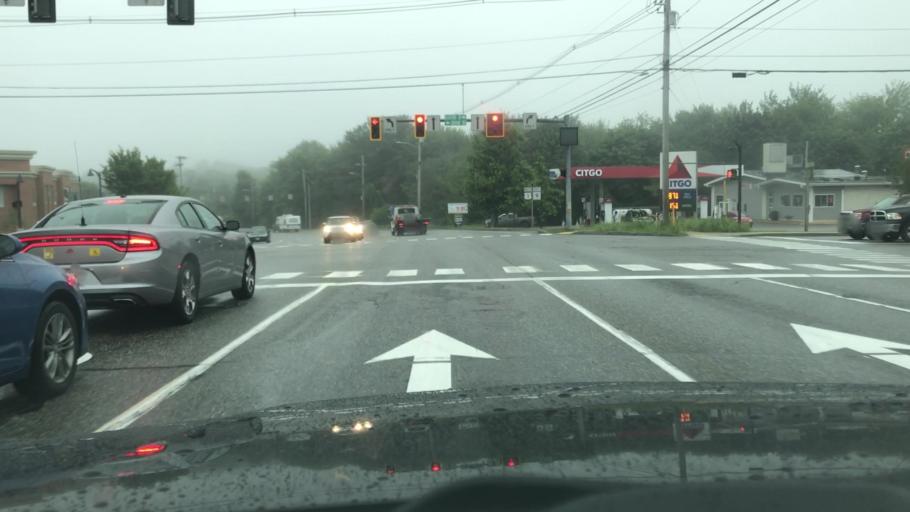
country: US
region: Maine
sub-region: Cumberland County
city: Scarborough
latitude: 43.5901
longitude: -70.3349
